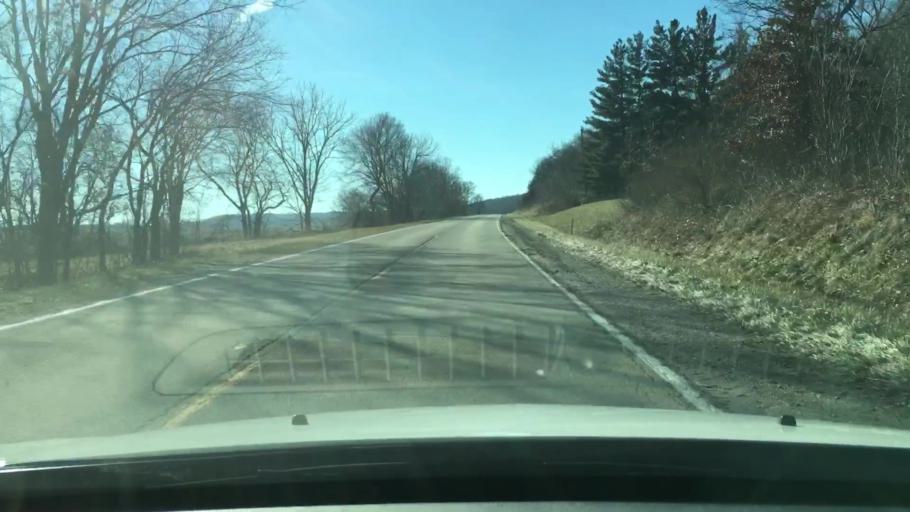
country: US
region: Illinois
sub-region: Mason County
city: Havana
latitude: 40.2530
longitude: -90.1819
